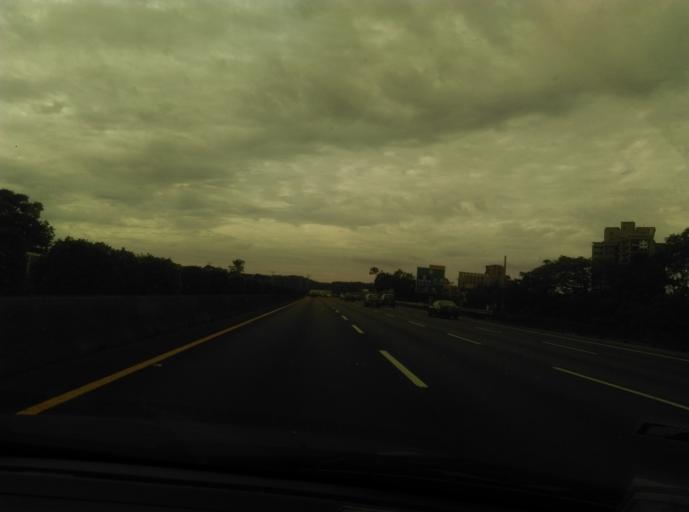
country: TW
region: Taiwan
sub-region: Taoyuan
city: Taoyuan
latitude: 24.9371
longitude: 121.3393
